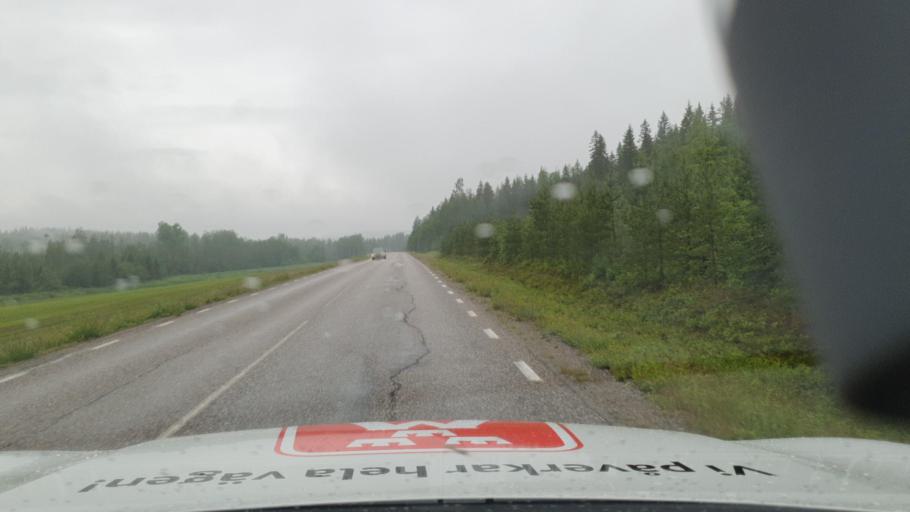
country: SE
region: Vaesterbotten
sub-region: Vannas Kommun
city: Vaennaes
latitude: 63.7759
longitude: 19.6036
